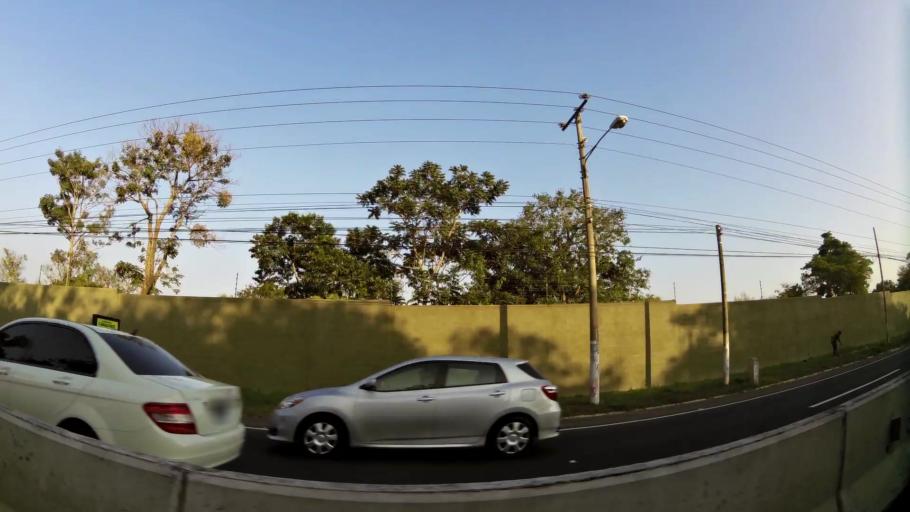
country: SV
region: La Libertad
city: Antiguo Cuscatlan
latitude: 13.6924
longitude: -89.2504
